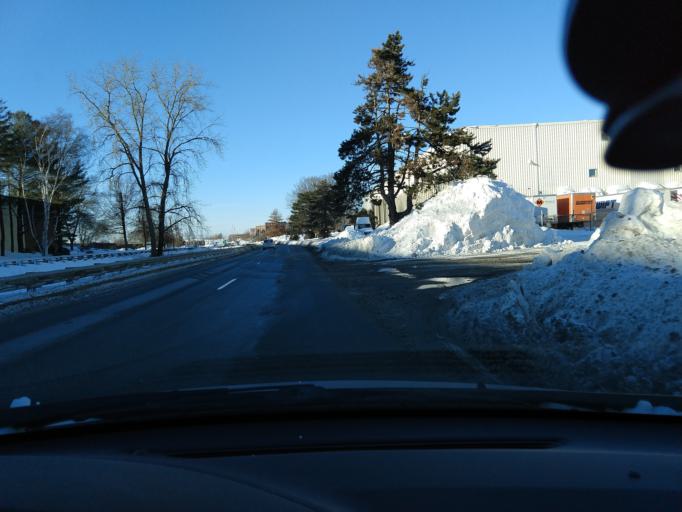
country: US
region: Massachusetts
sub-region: Middlesex County
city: Woburn
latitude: 42.5141
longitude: -71.1352
